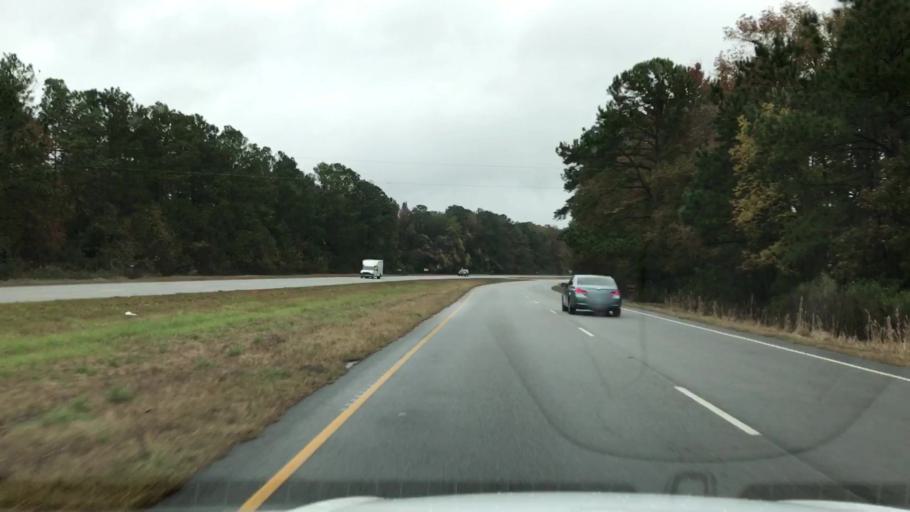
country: US
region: South Carolina
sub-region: Charleston County
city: Awendaw
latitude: 32.9349
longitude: -79.7122
